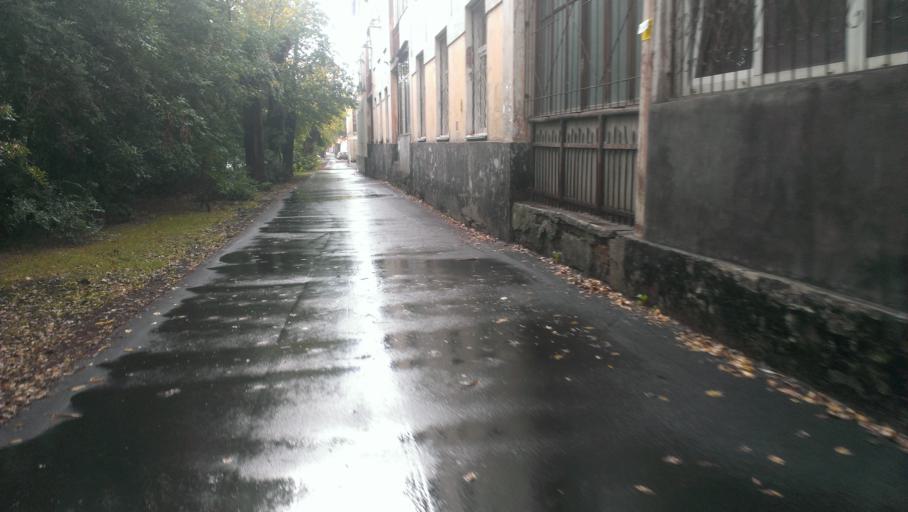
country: RU
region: Altai Krai
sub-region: Gorod Barnaulskiy
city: Barnaul
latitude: 53.3547
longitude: 83.7635
